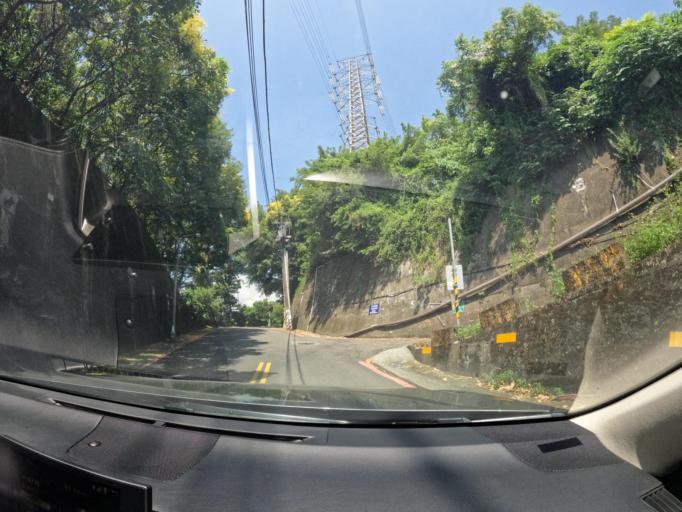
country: TW
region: Taipei
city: Taipei
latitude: 25.1171
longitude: 121.5398
